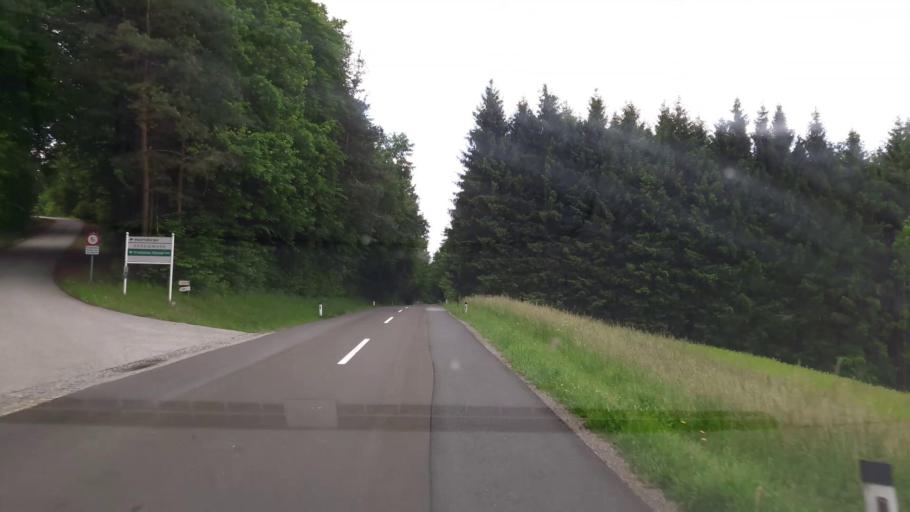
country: AT
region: Styria
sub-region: Politischer Bezirk Hartberg-Fuerstenfeld
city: Soechau
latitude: 47.0555
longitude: 16.0113
